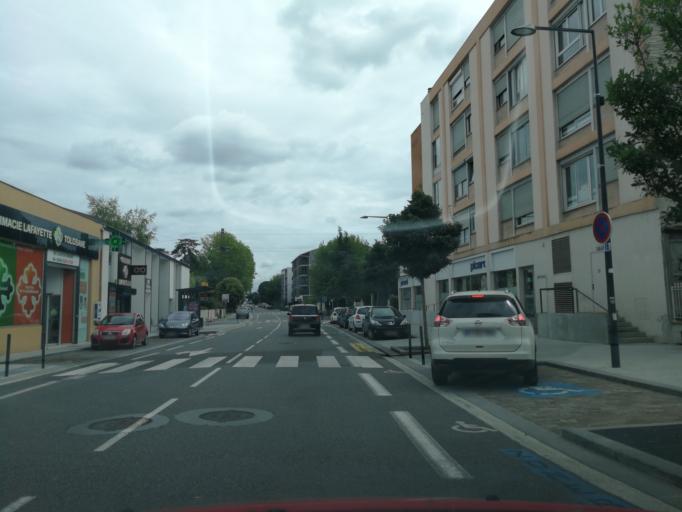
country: FR
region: Midi-Pyrenees
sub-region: Departement de la Haute-Garonne
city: Ramonville-Saint-Agne
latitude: 43.5512
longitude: 1.4700
